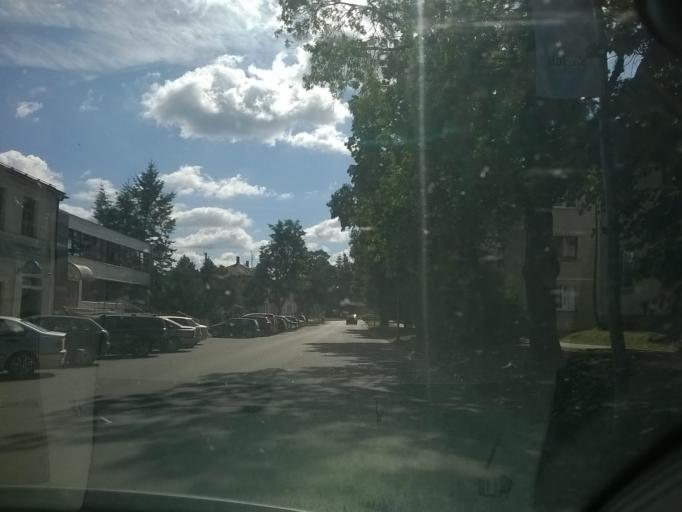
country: LV
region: Aluksnes Rajons
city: Aluksne
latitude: 57.4216
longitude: 27.0500
